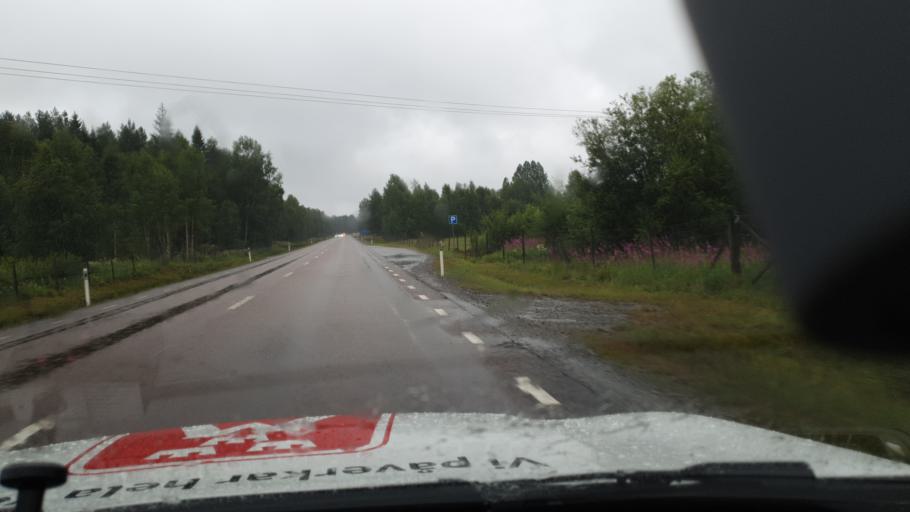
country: SE
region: Vaesterbotten
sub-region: Skelleftea Kommun
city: Burea
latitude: 64.6073
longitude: 21.1938
